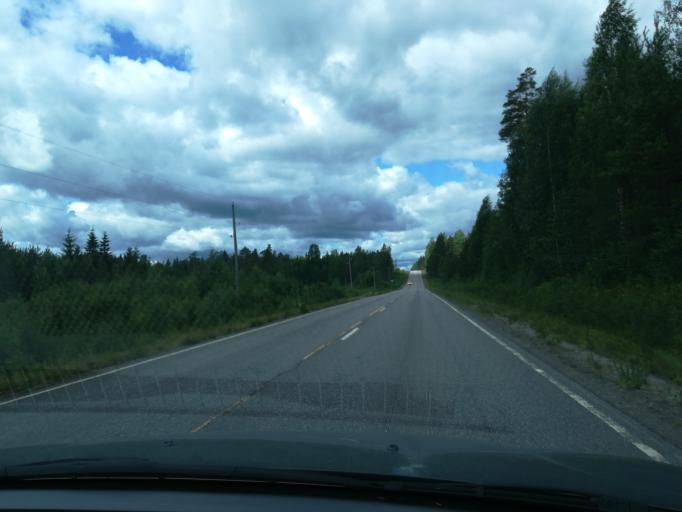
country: FI
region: Southern Savonia
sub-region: Mikkeli
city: Maentyharju
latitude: 61.3644
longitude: 26.9925
